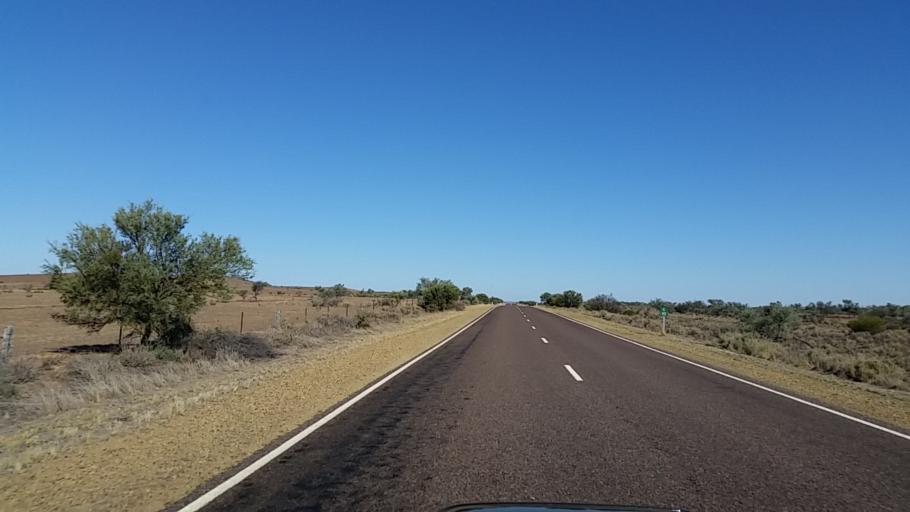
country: AU
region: South Australia
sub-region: Flinders Ranges
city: Quorn
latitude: -32.3437
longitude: 138.4846
